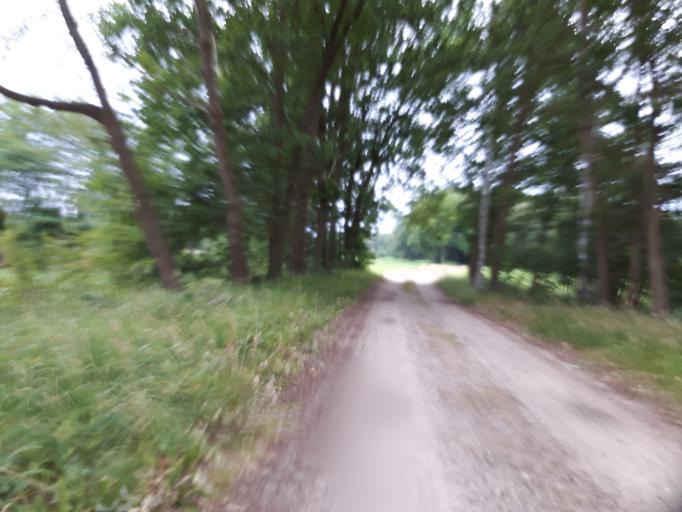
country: DE
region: Lower Saxony
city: Vierhofen
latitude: 53.2675
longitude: 10.1884
